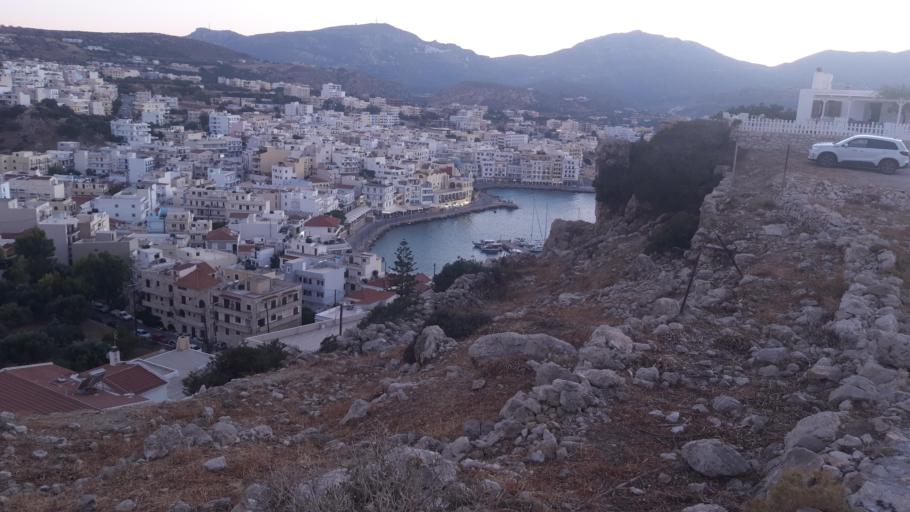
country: GR
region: South Aegean
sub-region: Nomos Dodekanisou
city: Karpathos
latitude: 35.5095
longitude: 27.2179
